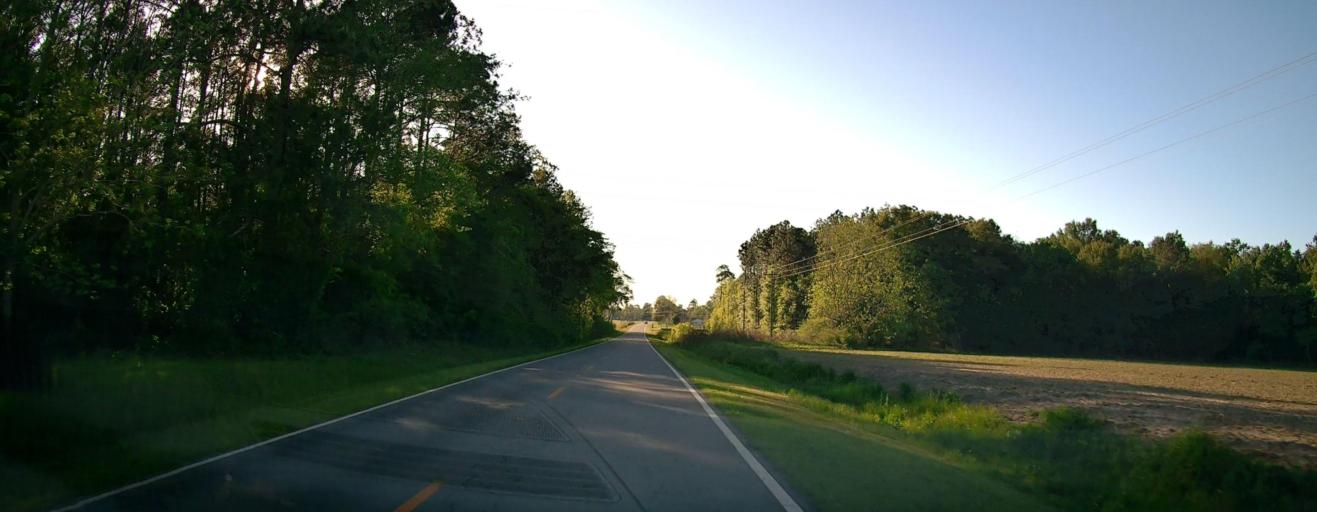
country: US
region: Georgia
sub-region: Ben Hill County
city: Fitzgerald
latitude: 31.6800
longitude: -83.1989
